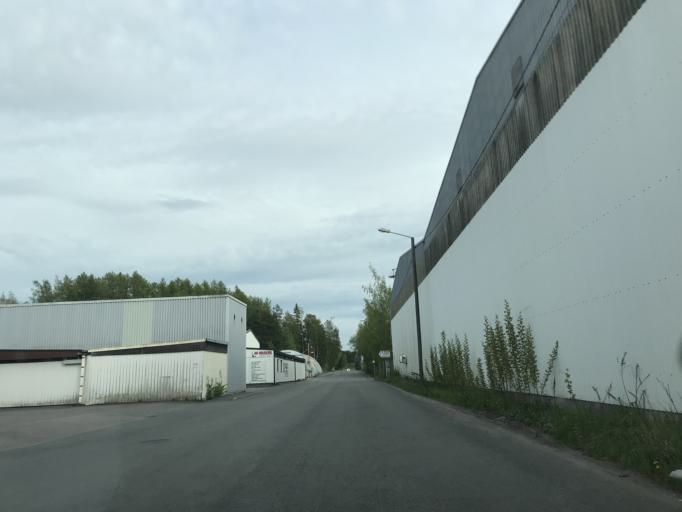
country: FI
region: Varsinais-Suomi
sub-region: Turku
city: Turku
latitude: 60.4477
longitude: 22.3073
